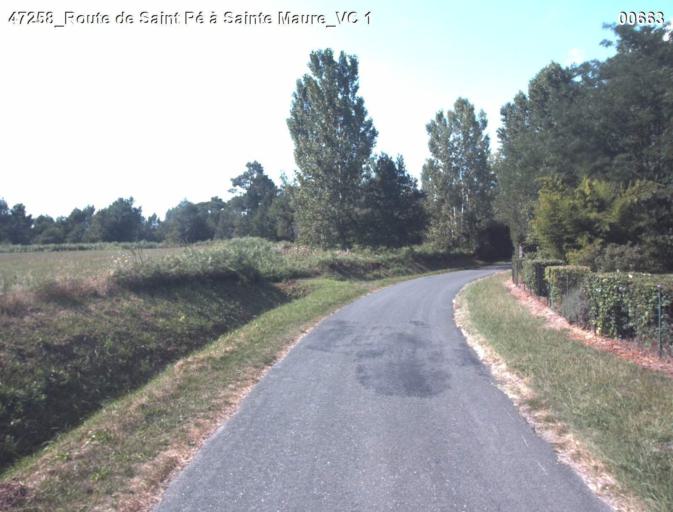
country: FR
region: Midi-Pyrenees
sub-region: Departement du Gers
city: Montreal
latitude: 44.0157
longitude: 0.1295
